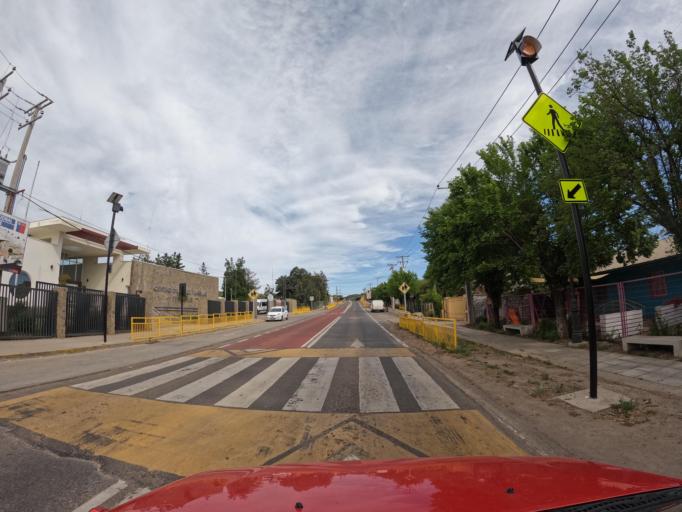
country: CL
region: Maule
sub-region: Provincia de Talca
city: Talca
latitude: -35.3976
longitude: -71.7986
